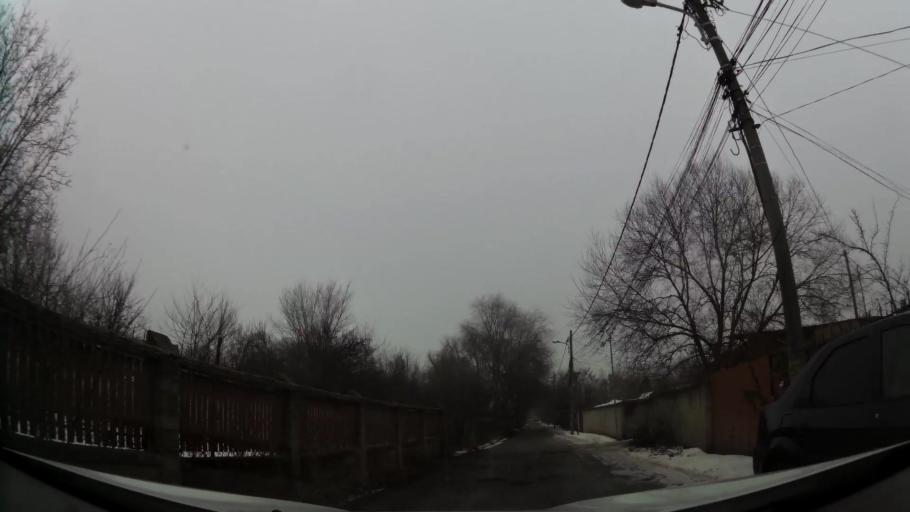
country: RO
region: Ilfov
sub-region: Comuna Chiajna
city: Rosu
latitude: 44.4444
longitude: 26.0162
